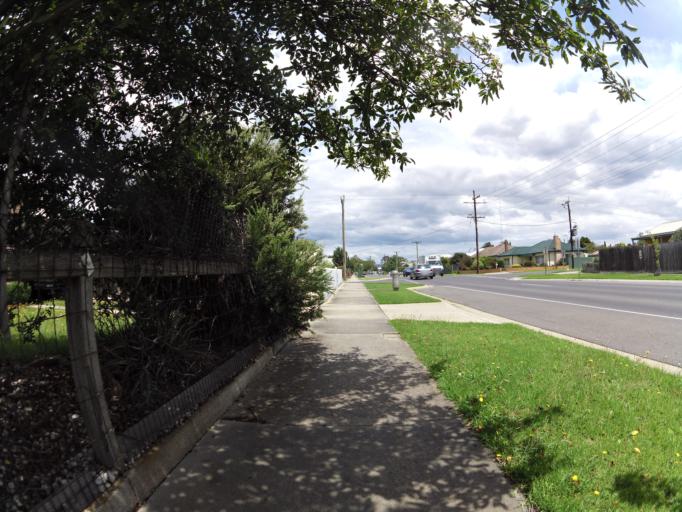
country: AU
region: Victoria
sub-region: Latrobe
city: Traralgon
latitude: -38.1908
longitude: 146.5341
